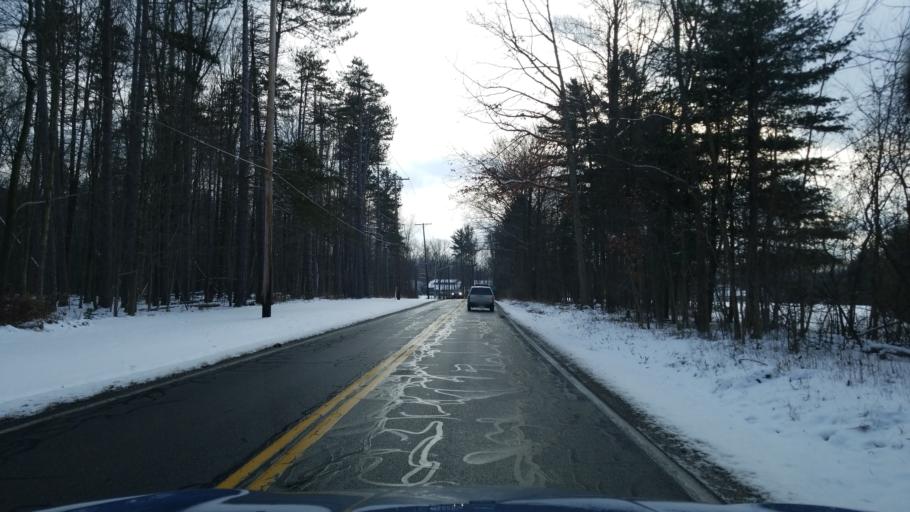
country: US
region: Ohio
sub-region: Cuyahoga County
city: Strongsville
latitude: 41.3386
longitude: -81.8450
